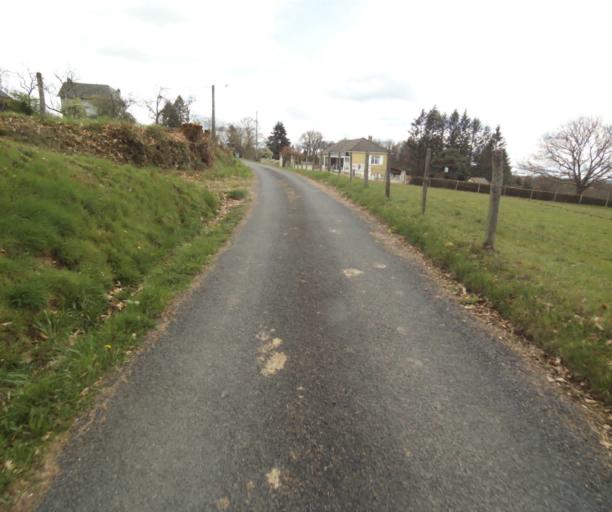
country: FR
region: Limousin
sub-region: Departement de la Correze
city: Laguenne
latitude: 45.2069
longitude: 1.8754
